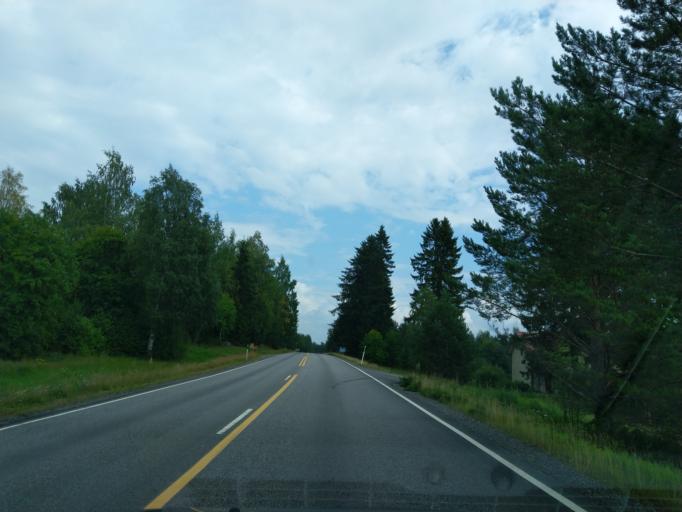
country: FI
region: South Karelia
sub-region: Imatra
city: Parikkala
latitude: 61.6037
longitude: 29.4709
